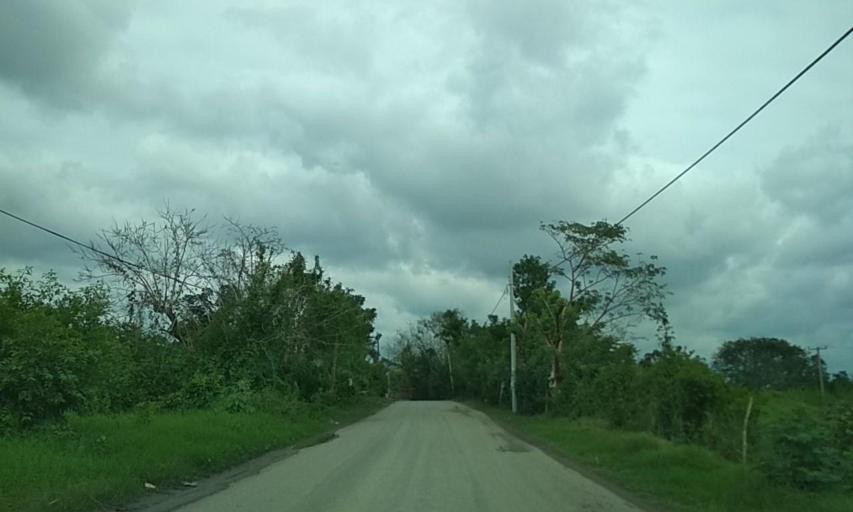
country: MX
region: Veracruz
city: Agua Dulce
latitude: 20.3607
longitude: -97.3343
